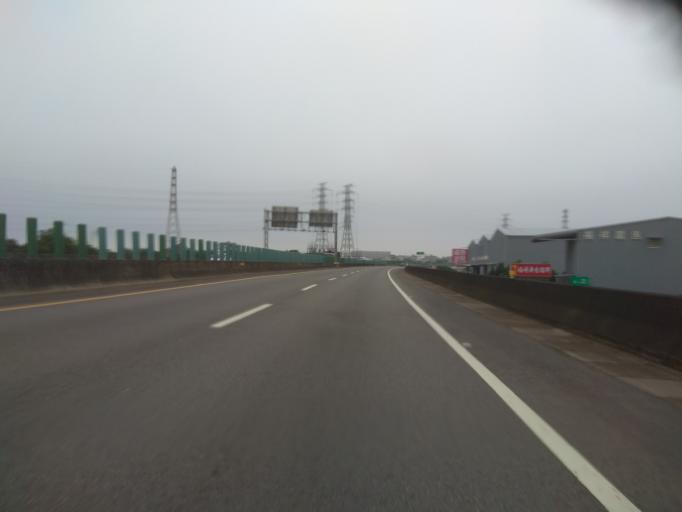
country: TW
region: Taiwan
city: Taoyuan City
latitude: 24.9840
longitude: 121.1290
